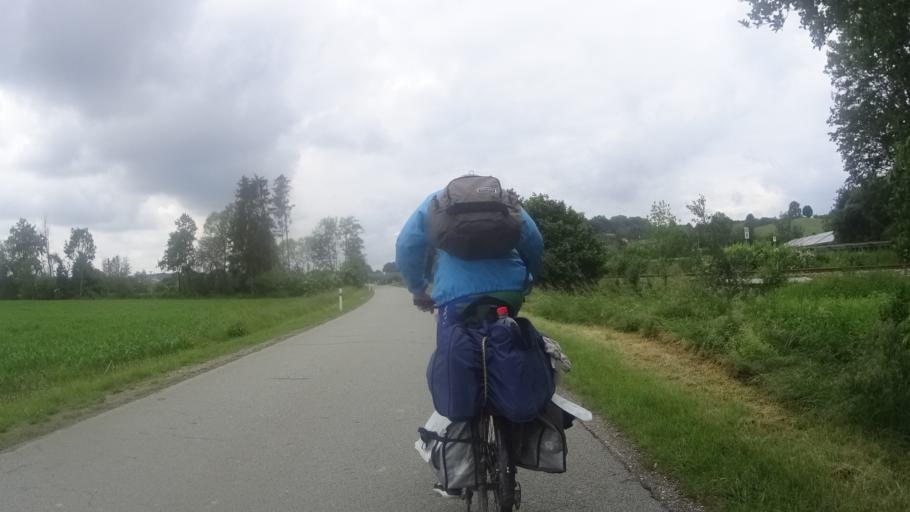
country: DE
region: Bavaria
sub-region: Lower Bavaria
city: Pfarrkirchen
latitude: 48.4347
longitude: 12.9694
